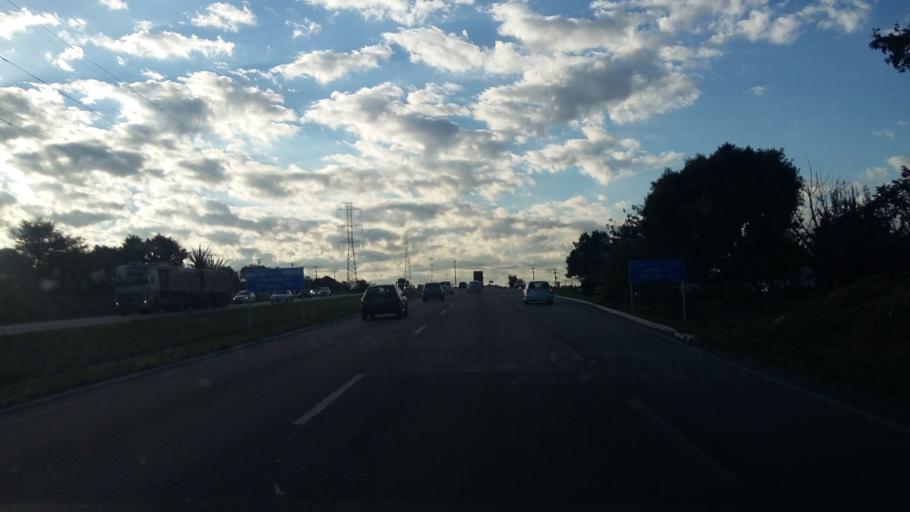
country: BR
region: Parana
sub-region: Curitiba
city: Curitiba
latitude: -25.4887
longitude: -49.3456
